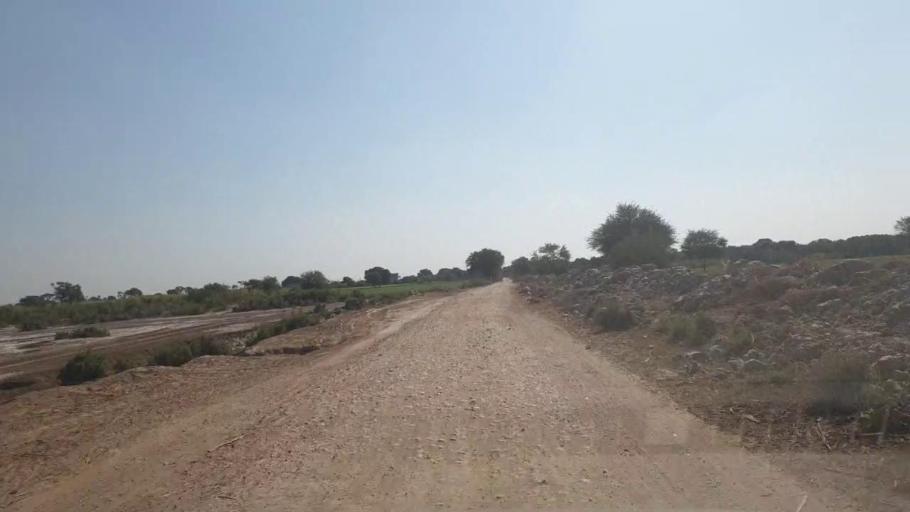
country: PK
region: Sindh
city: Chambar
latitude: 25.3148
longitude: 68.7409
